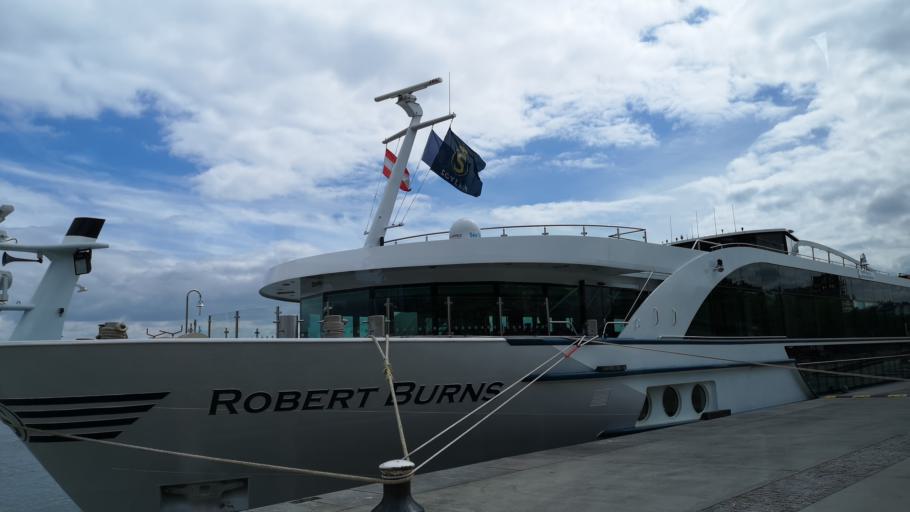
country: AT
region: Vienna
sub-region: Wien Stadt
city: Vienna
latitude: 48.2238
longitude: 16.4091
